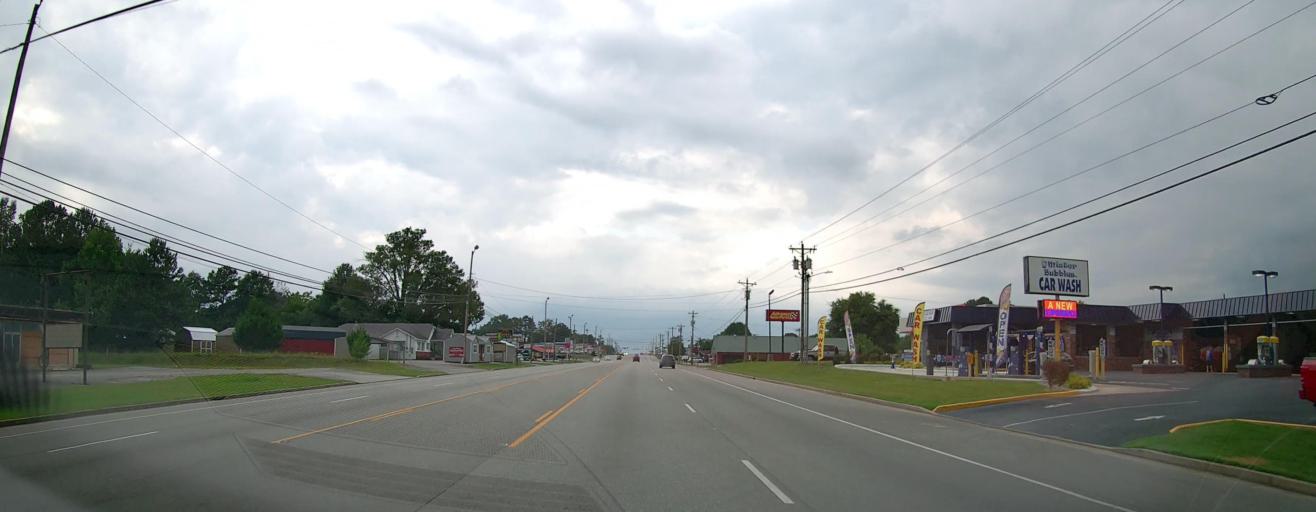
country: US
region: Tennessee
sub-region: Coffee County
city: Manchester
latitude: 35.4647
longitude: -86.0678
